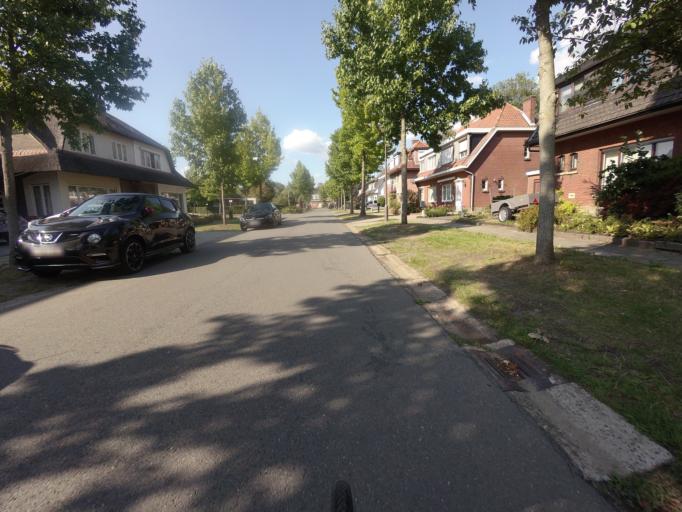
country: BE
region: Flanders
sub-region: Provincie Antwerpen
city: Kapellen
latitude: 51.2823
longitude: 4.4390
